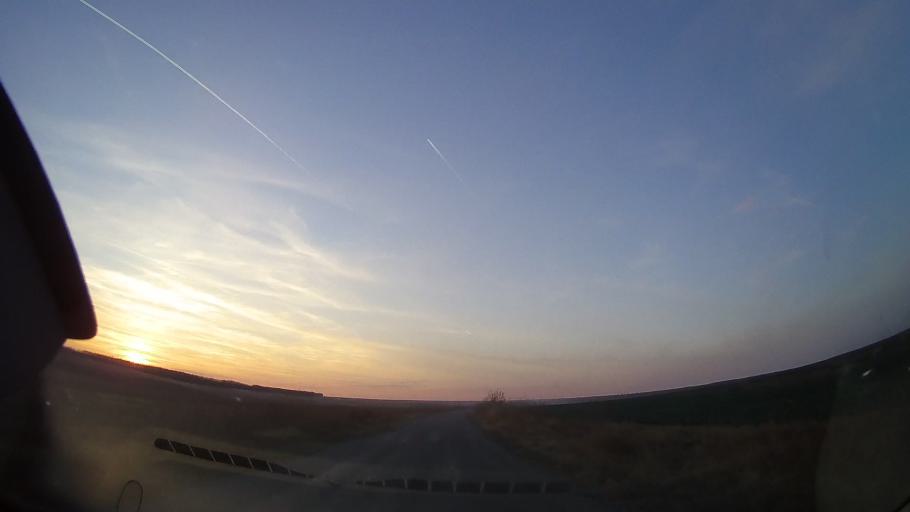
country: RO
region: Constanta
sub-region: Comuna Mereni
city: Mereni
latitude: 44.0159
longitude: 28.3102
